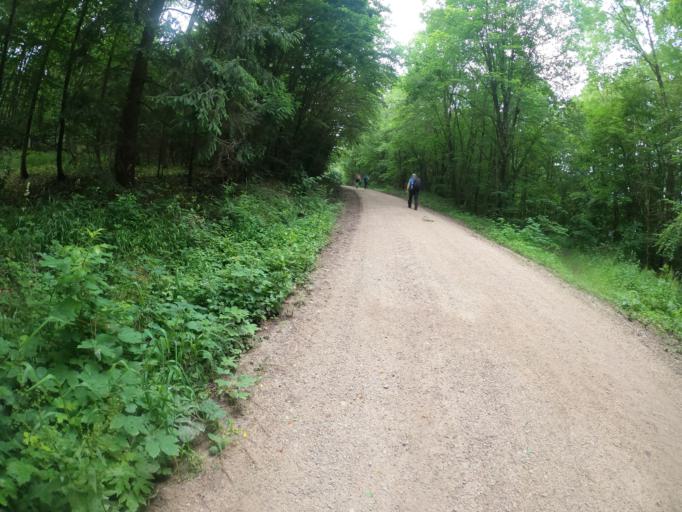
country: DE
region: Bavaria
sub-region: Upper Franconia
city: Litzendorf
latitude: 49.9251
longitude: 11.0327
